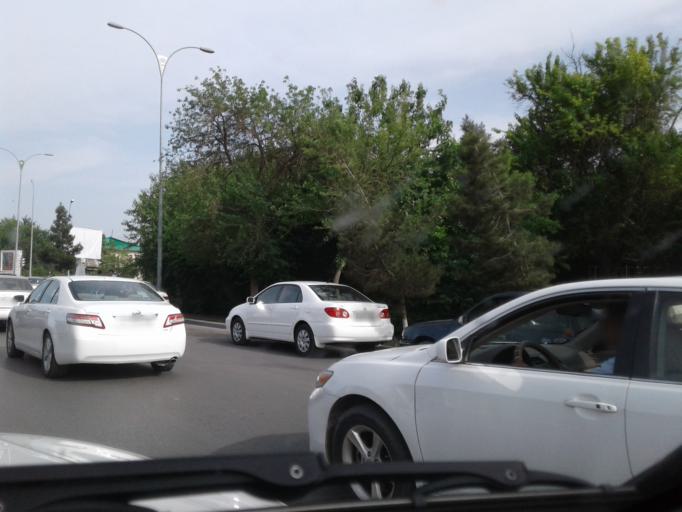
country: TM
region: Mary
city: Mary
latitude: 37.5903
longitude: 61.8323
